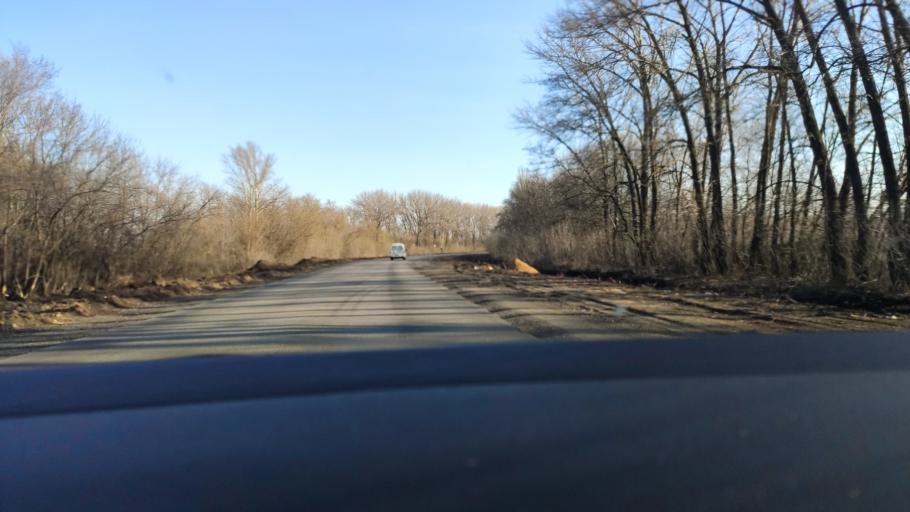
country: RU
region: Voronezj
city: Uryv-Pokrovka
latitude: 51.1931
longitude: 39.0862
